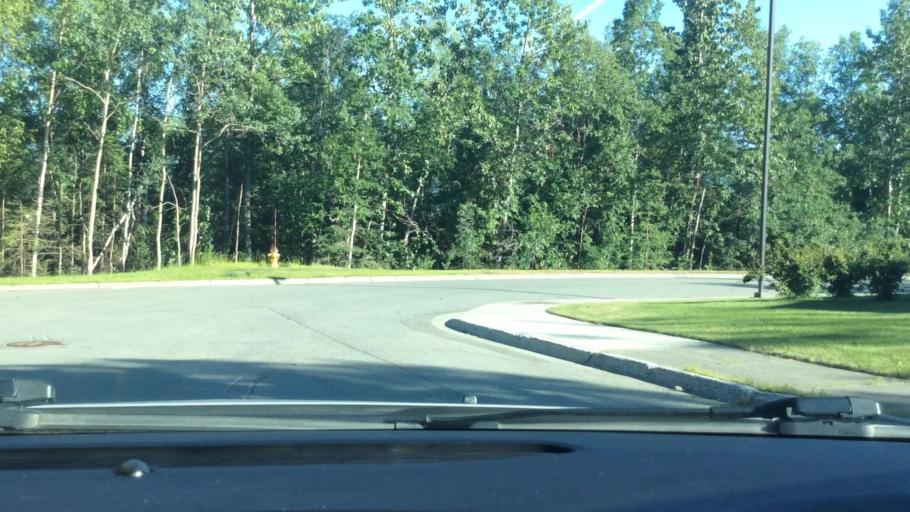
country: US
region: Alaska
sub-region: Anchorage Municipality
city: Elmendorf Air Force Base
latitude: 61.2516
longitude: -149.7004
